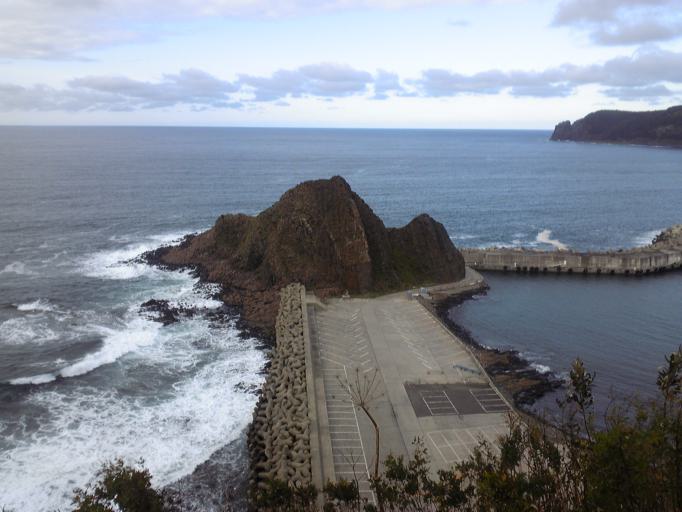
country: JP
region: Hokkaido
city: Shibetsu
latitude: 44.0738
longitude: 144.9908
